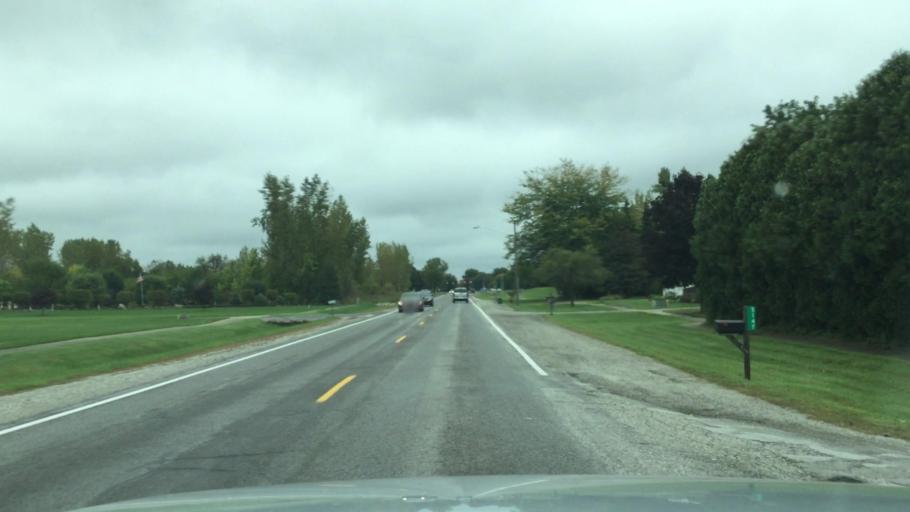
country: US
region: Michigan
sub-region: Saginaw County
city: Carrollton
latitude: 43.4703
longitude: -83.9952
